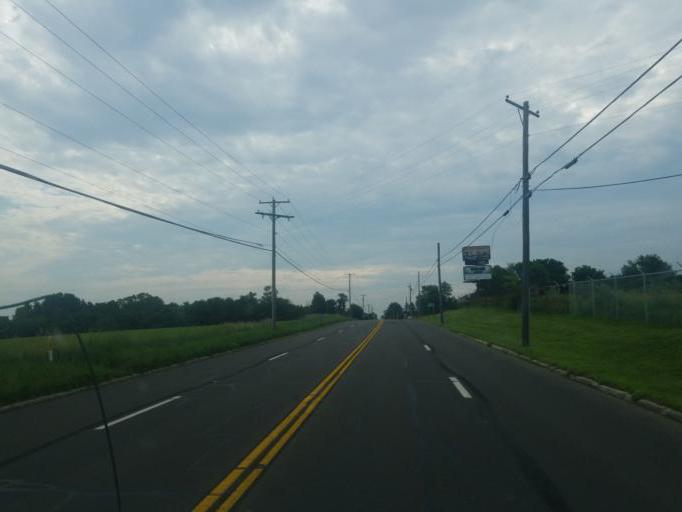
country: US
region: Ohio
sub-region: Wayne County
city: Dalton
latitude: 40.7989
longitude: -81.6355
